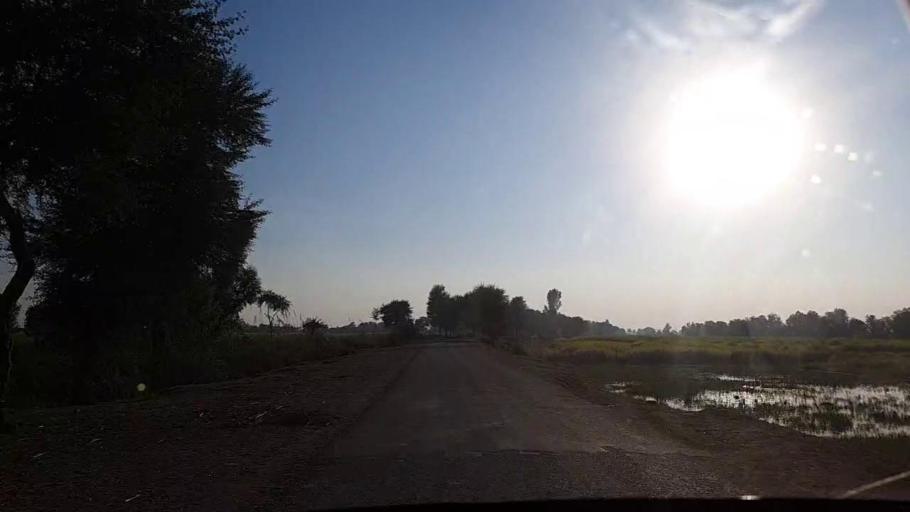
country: PK
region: Sindh
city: Sobhadero
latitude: 27.4192
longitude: 68.4041
